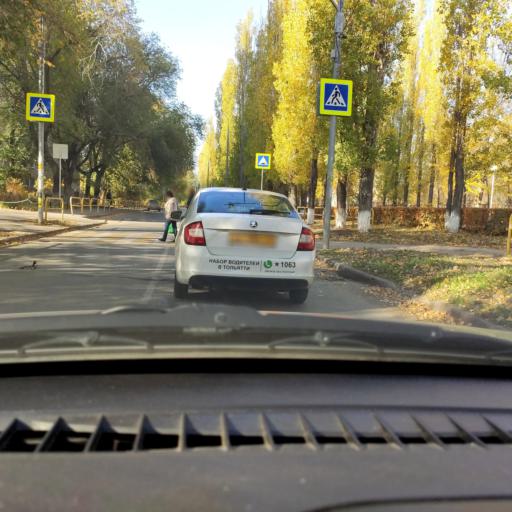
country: RU
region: Samara
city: Tol'yatti
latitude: 53.5248
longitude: 49.2678
